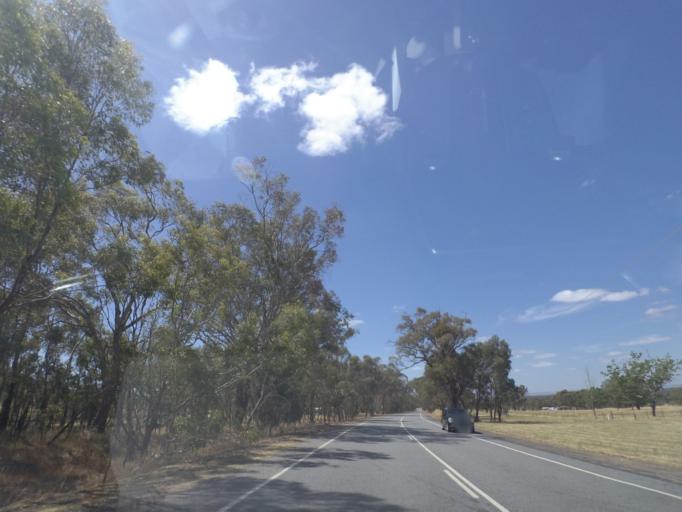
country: AU
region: Victoria
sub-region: Wangaratta
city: Wangaratta
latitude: -36.4501
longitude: 146.2385
